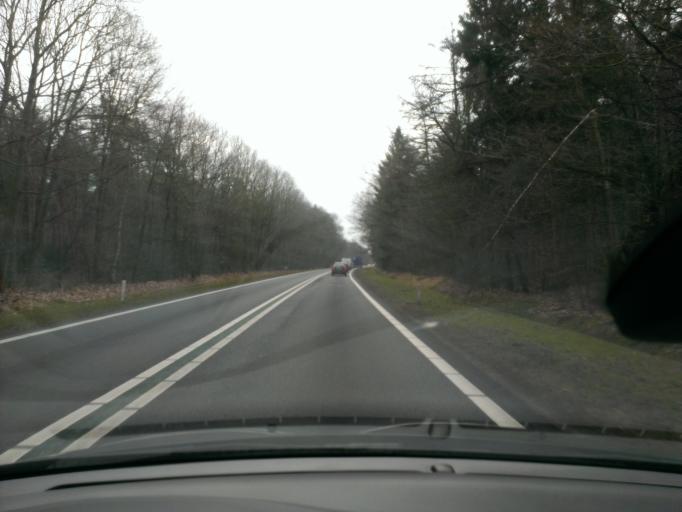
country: NL
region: Overijssel
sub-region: Gemeente Twenterand
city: Magele
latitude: 52.5444
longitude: 6.5436
